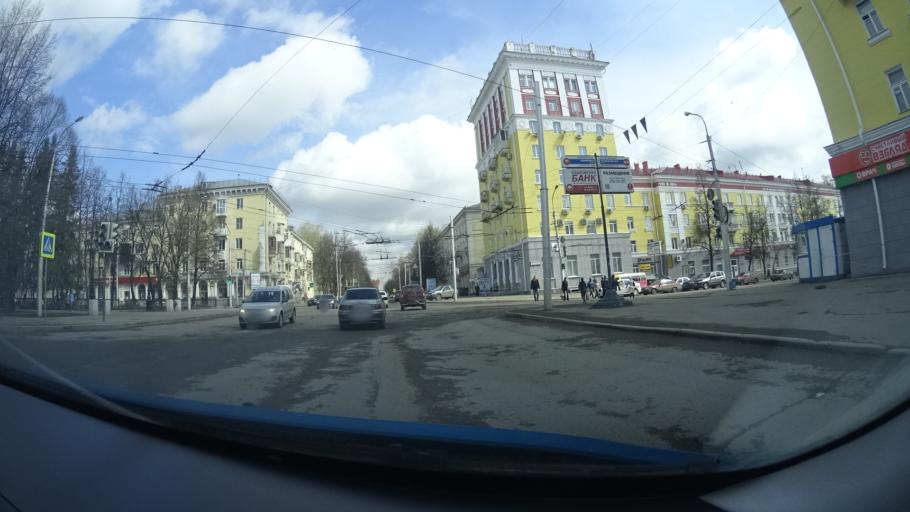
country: RU
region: Bashkortostan
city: Ufa
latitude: 54.8172
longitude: 56.0745
